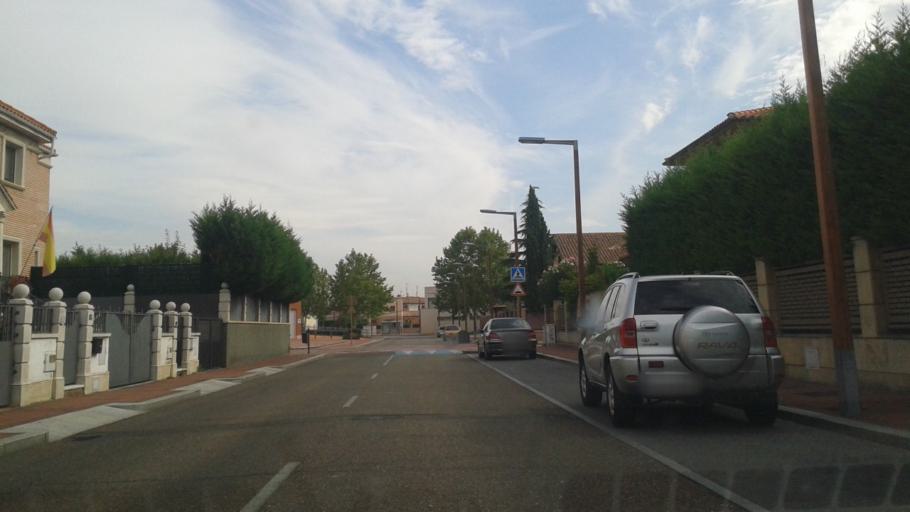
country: ES
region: Castille and Leon
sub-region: Provincia de Valladolid
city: Arroyo
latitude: 41.6116
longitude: -4.7849
